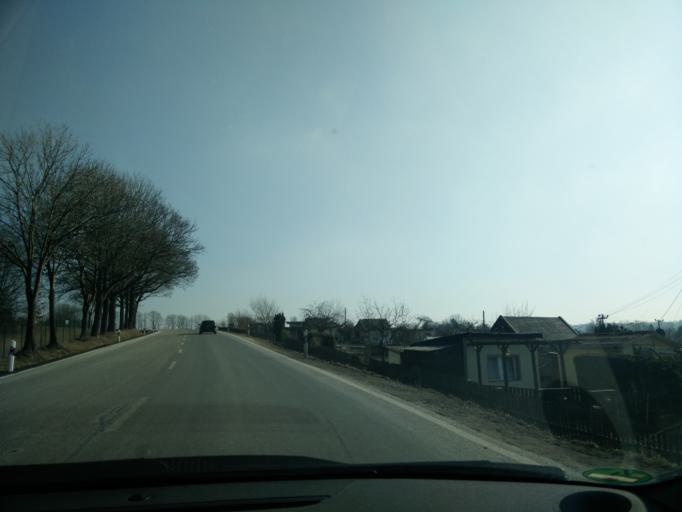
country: DE
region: Saxony
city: Muhlau
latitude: 50.8984
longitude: 12.7612
